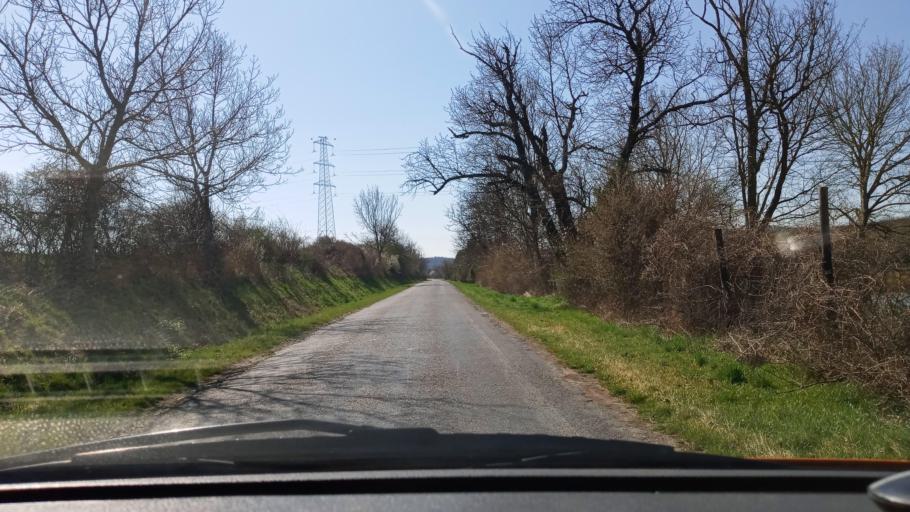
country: HU
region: Baranya
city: Kozarmisleny
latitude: 46.0470
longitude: 18.3821
